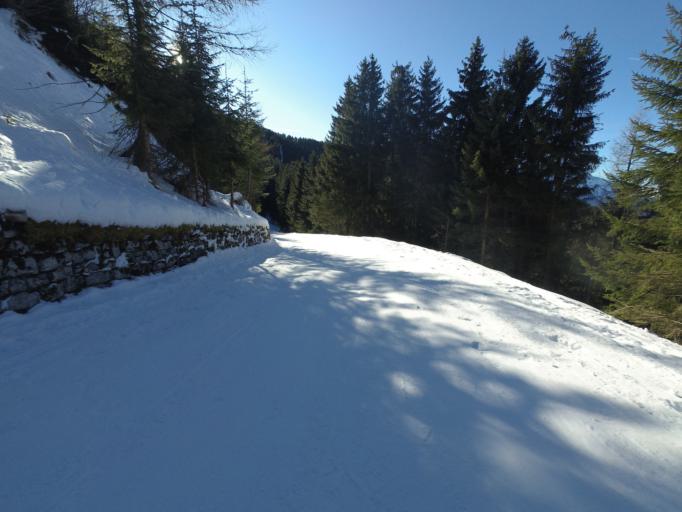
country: AT
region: Salzburg
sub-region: Politischer Bezirk Hallein
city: Scheffau am Tennengebirge
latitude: 47.6395
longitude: 13.2551
